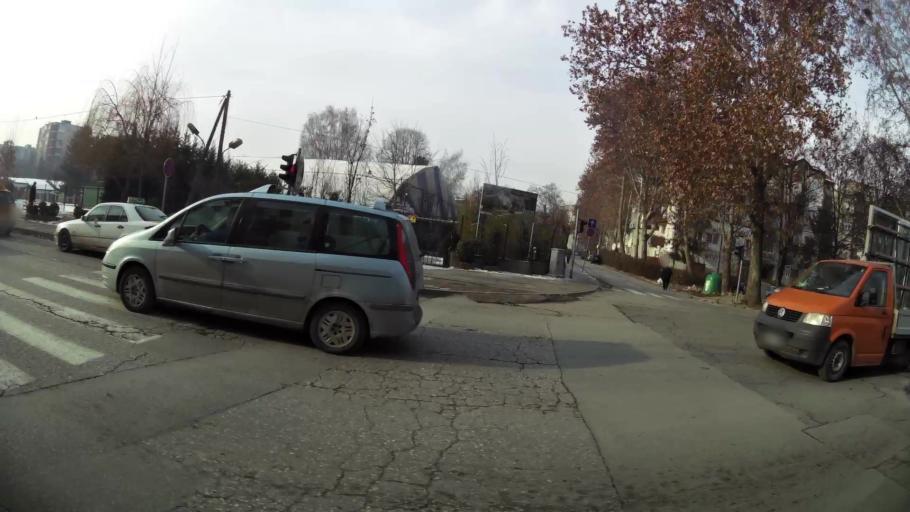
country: MK
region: Cair
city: Cair
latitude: 42.0202
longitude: 21.4346
